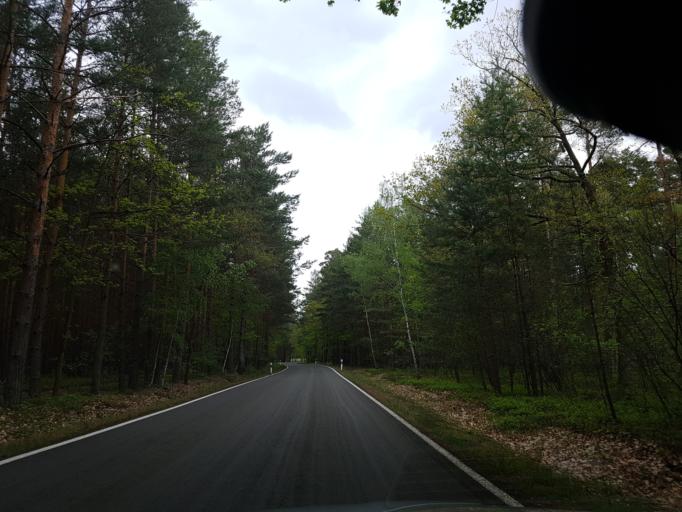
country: DE
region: Brandenburg
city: Crinitz
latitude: 51.7520
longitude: 13.7522
